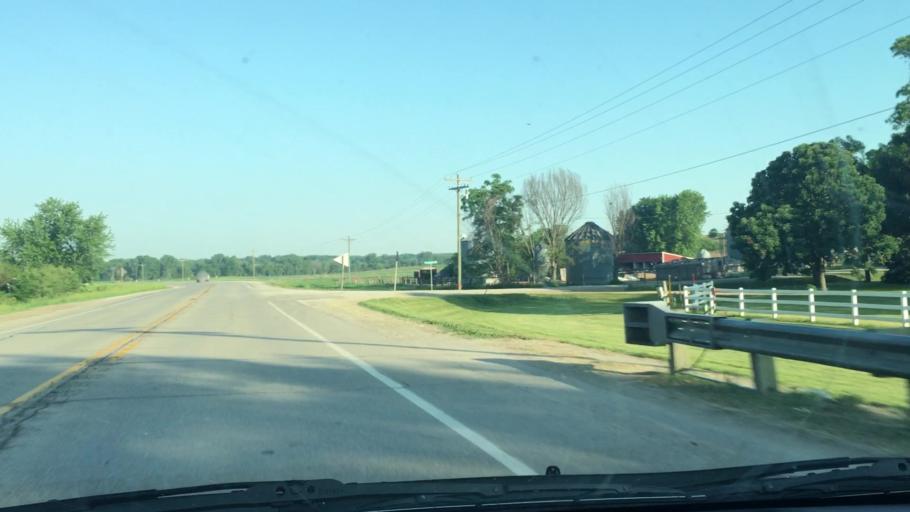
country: US
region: Iowa
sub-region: Johnson County
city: Tiffin
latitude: 41.7126
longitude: -91.7000
